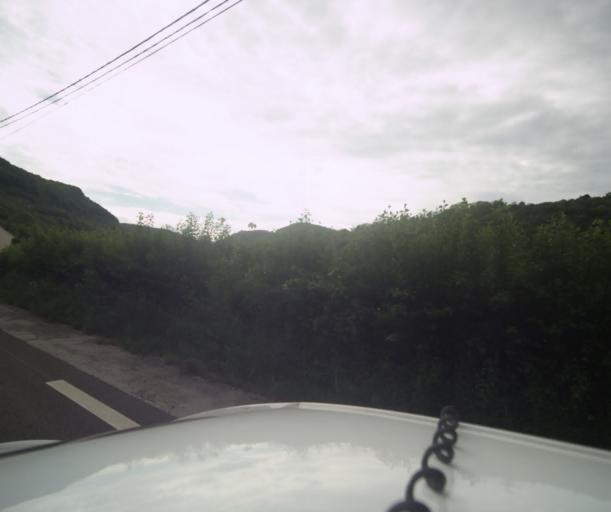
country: FR
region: Franche-Comte
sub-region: Departement du Doubs
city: Beure
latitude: 47.2199
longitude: 6.0298
